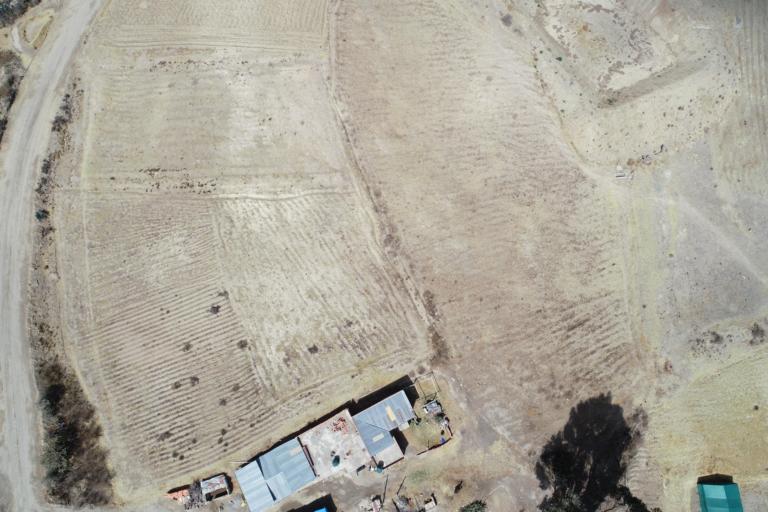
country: BO
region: La Paz
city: La Paz
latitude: -16.5991
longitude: -68.1282
